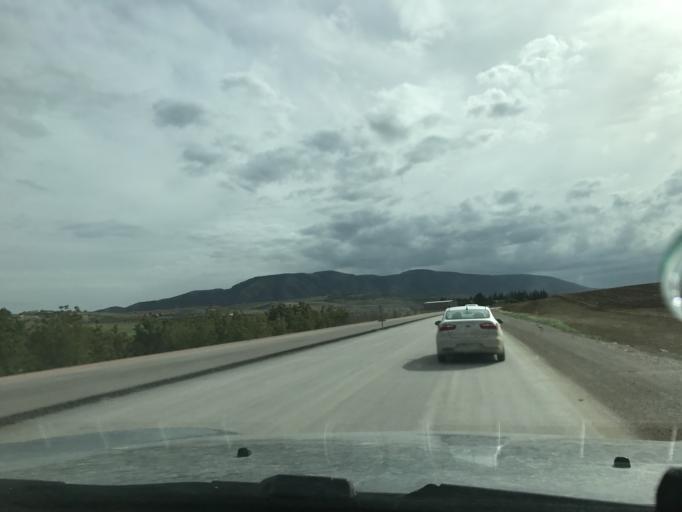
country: TN
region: Silyanah
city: Bu `Aradah
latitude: 36.1474
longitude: 9.6313
